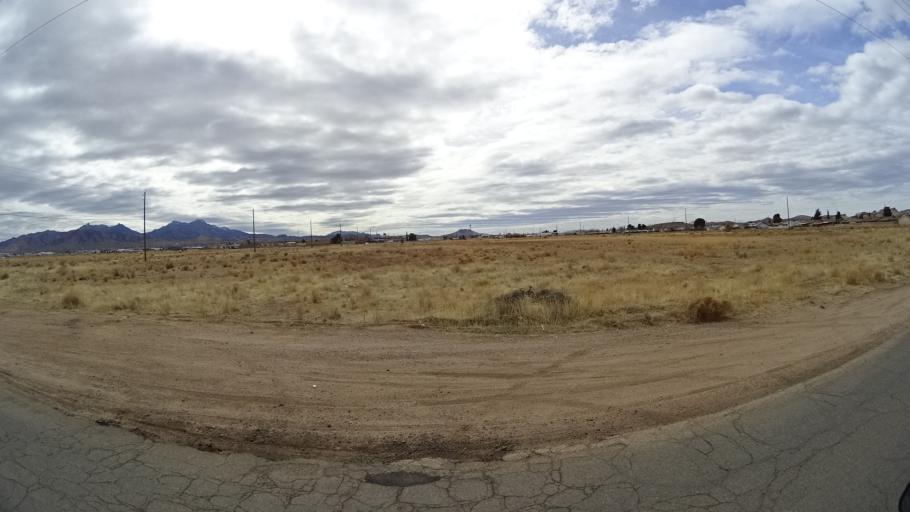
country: US
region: Arizona
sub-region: Mohave County
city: New Kingman-Butler
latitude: 35.2323
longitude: -114.0156
